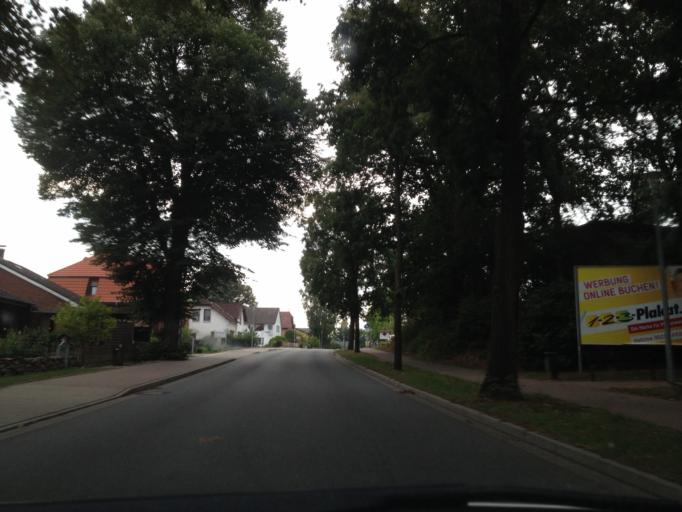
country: DE
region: Schleswig-Holstein
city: Rickling
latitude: 54.0000
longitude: 10.1690
